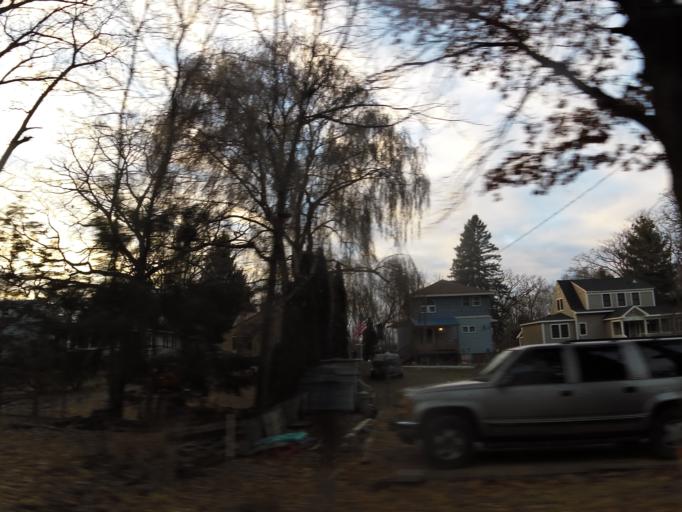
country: US
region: Minnesota
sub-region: Washington County
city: Mahtomedi
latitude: 45.0690
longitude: -92.9565
